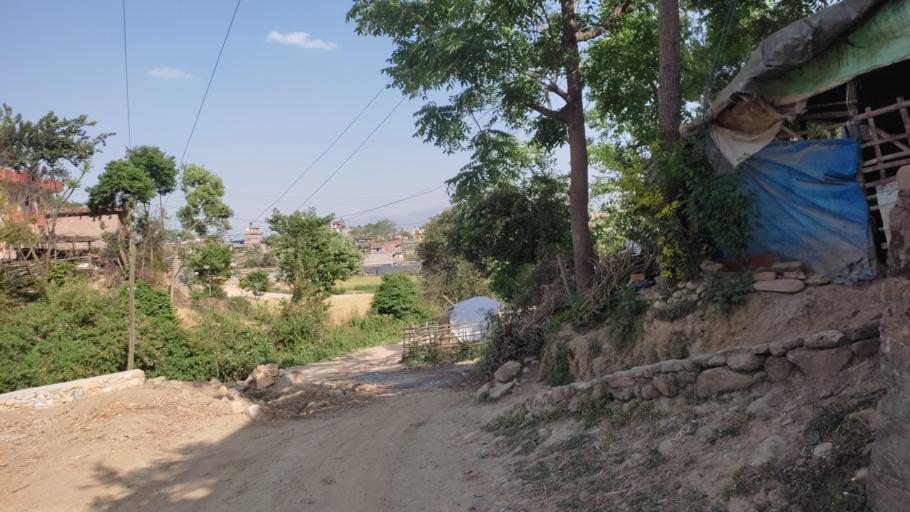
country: NP
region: Central Region
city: Kirtipur
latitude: 27.6598
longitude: 85.2639
